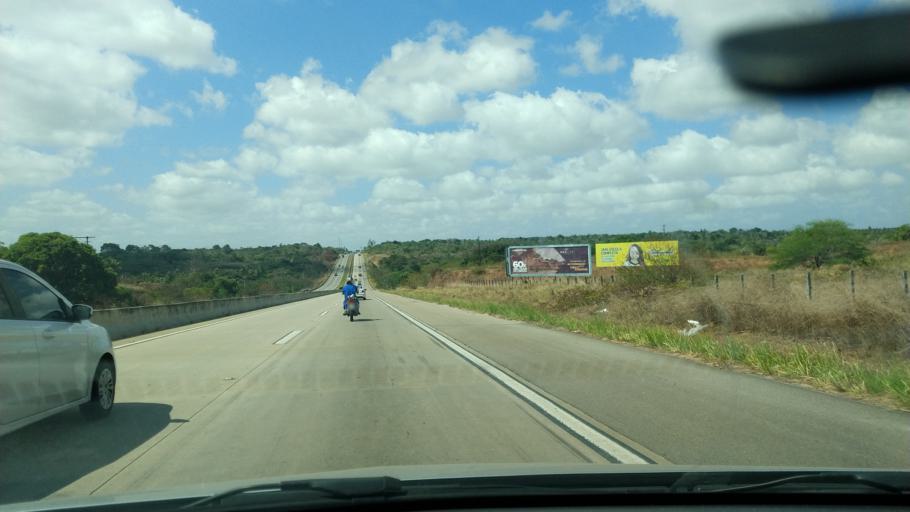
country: BR
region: Rio Grande do Norte
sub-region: Parnamirim
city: Parnamirim
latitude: -5.9655
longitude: -35.2648
